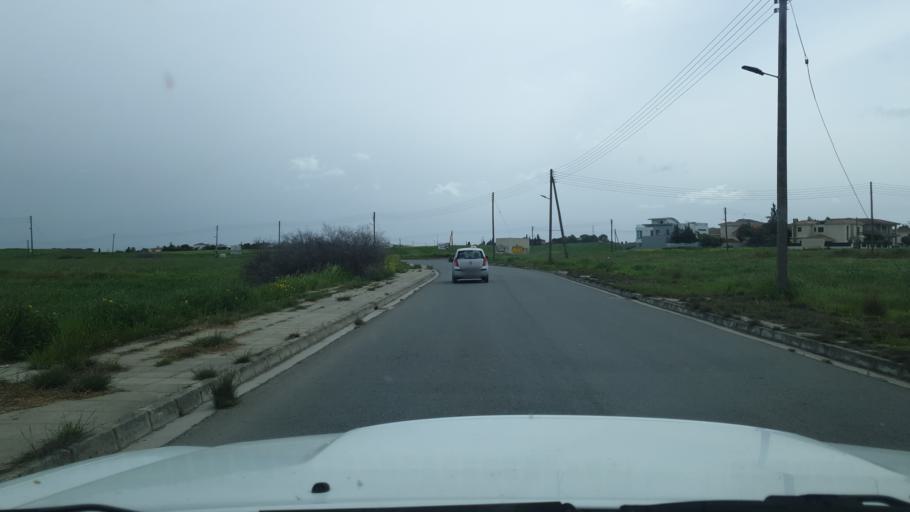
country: CY
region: Lefkosia
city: Tseri
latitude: 35.1021
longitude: 33.3533
